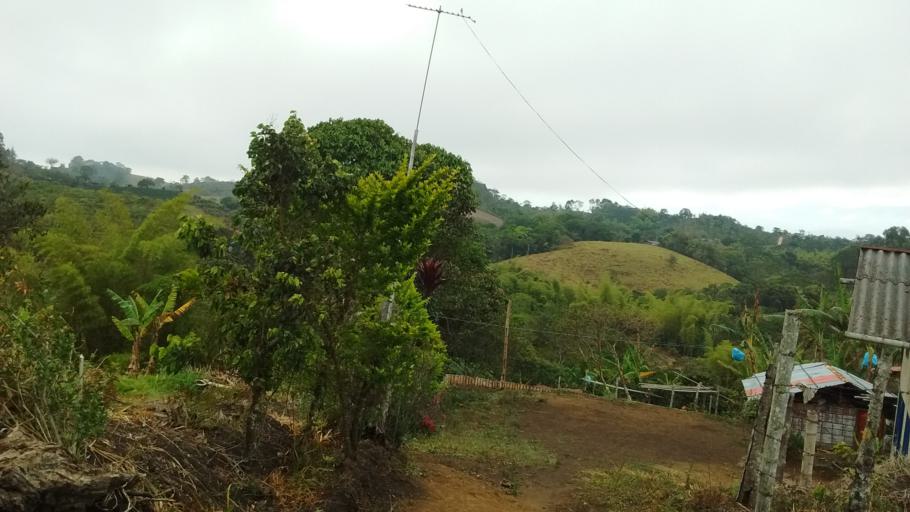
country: CO
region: Cauca
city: Lopez
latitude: 2.3914
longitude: -76.7481
